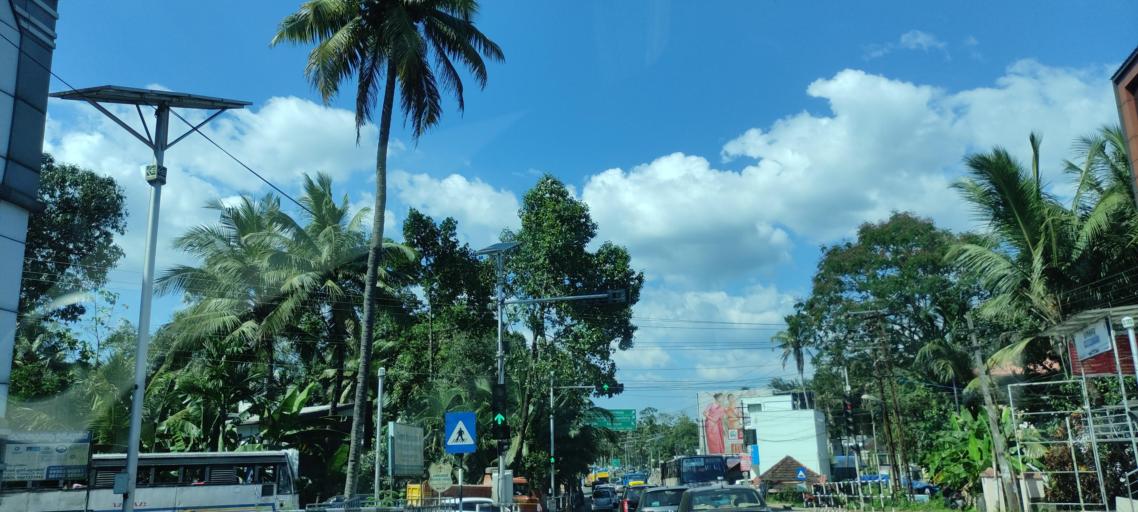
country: IN
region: Kerala
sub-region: Pattanamtitta
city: Adur
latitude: 9.1445
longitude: 76.7329
